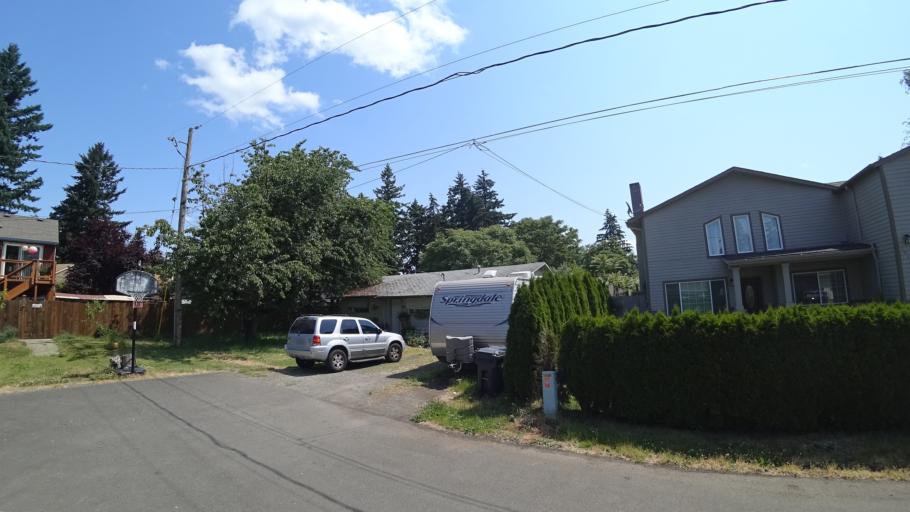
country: US
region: Oregon
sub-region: Clackamas County
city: Oatfield
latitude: 45.4493
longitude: -122.5919
